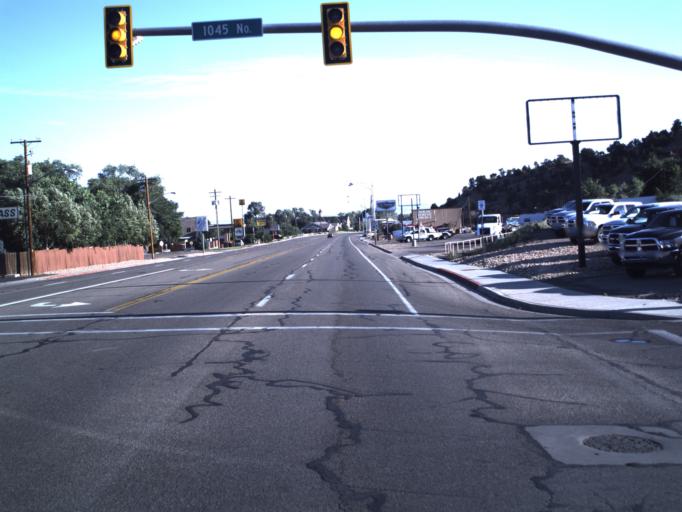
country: US
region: Utah
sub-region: Iron County
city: Cedar City
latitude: 37.6952
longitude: -113.0627
